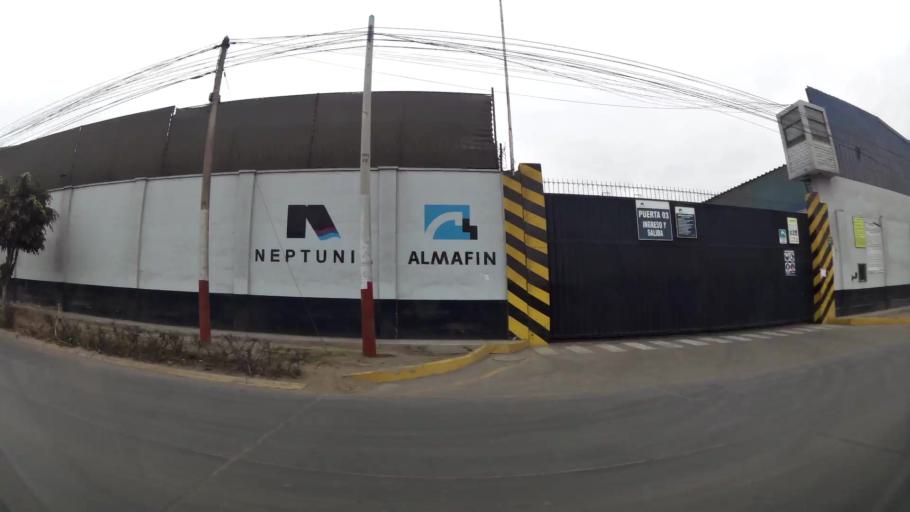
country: PE
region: Callao
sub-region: Callao
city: Callao
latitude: -12.0501
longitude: -77.1189
